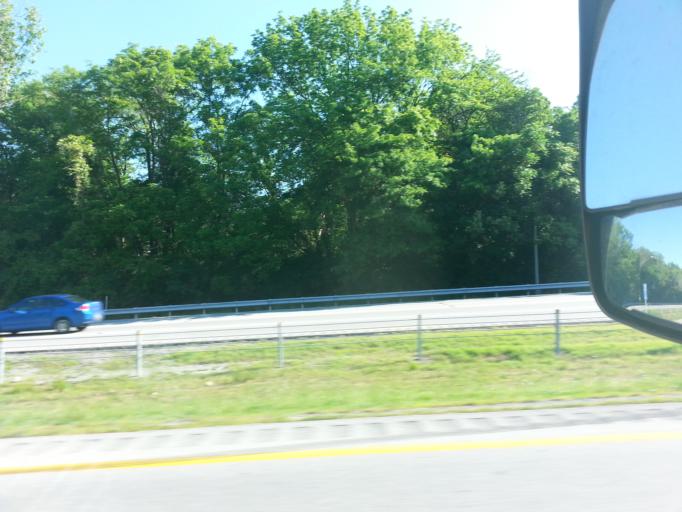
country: US
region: Indiana
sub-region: Clark County
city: Jeffersonville
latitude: 38.2485
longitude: -85.7040
